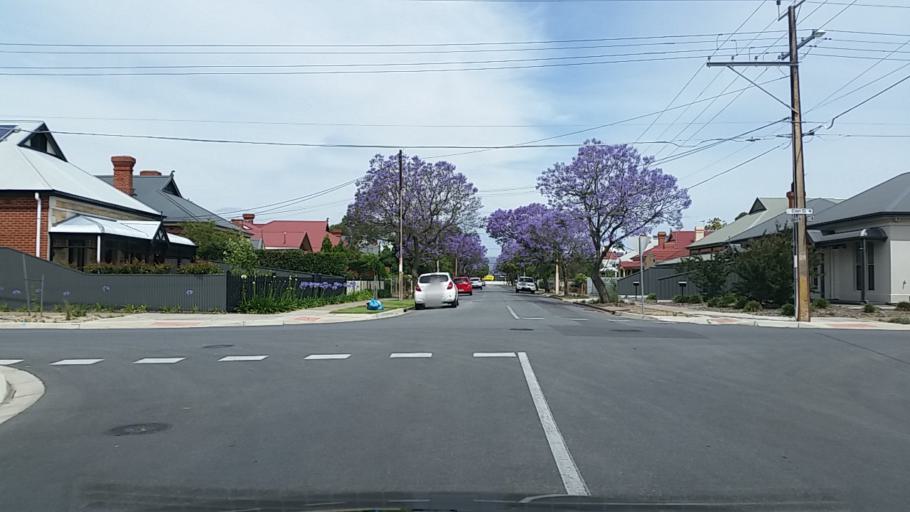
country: AU
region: South Australia
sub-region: Charles Sturt
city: Allenby Gardens
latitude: -34.8915
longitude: 138.5654
